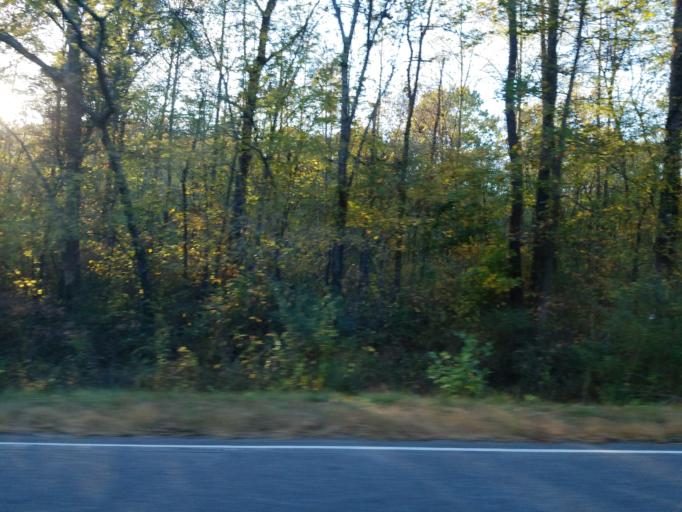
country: US
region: Georgia
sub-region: Bartow County
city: Adairsville
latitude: 34.2660
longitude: -84.9584
